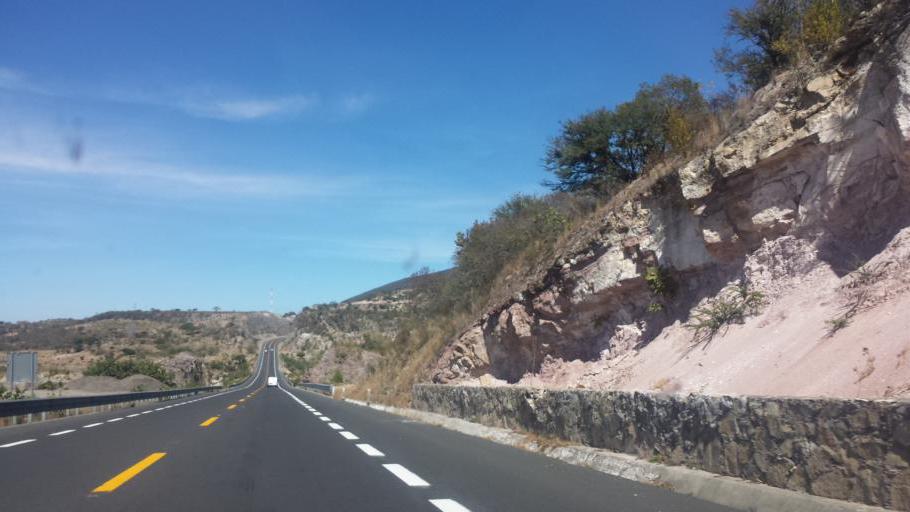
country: MX
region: Oaxaca
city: San Gabriel Casa Blanca
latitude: 17.9688
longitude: -97.3575
